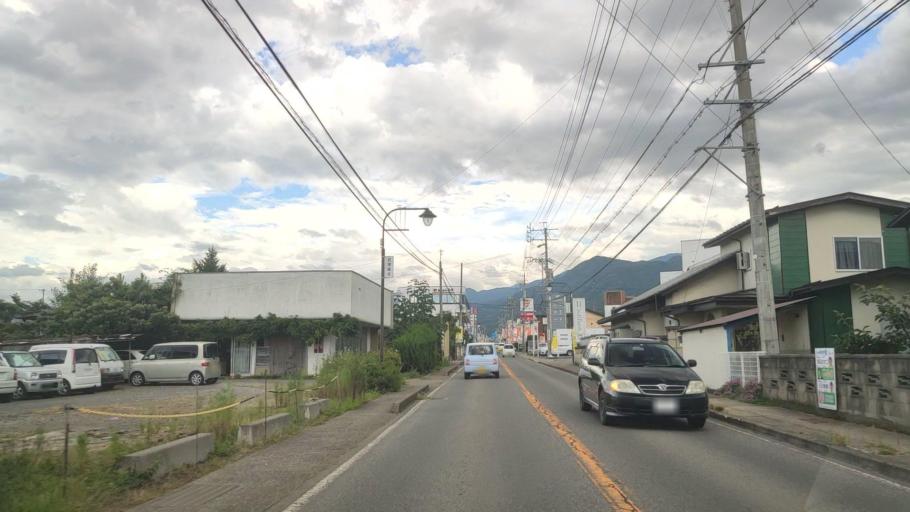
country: JP
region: Nagano
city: Suzaka
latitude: 36.6546
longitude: 138.2985
